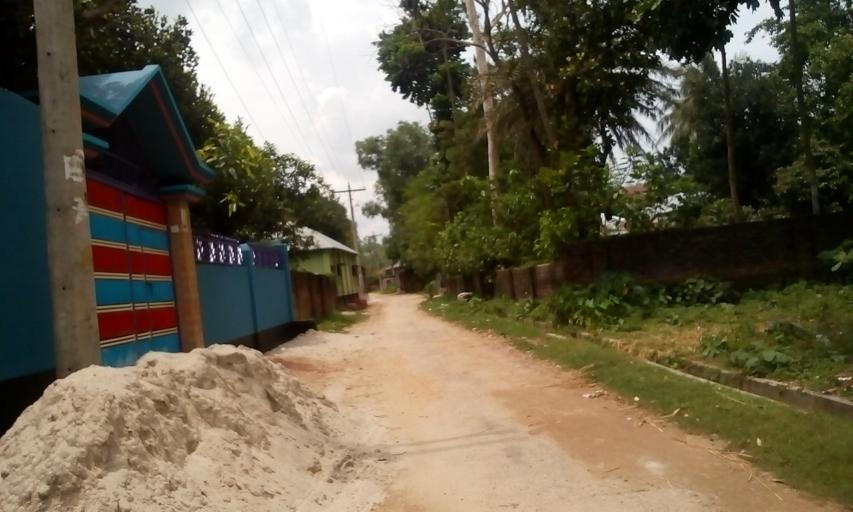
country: BD
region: Rangpur Division
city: Parbatipur
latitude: 25.3999
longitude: 88.9897
